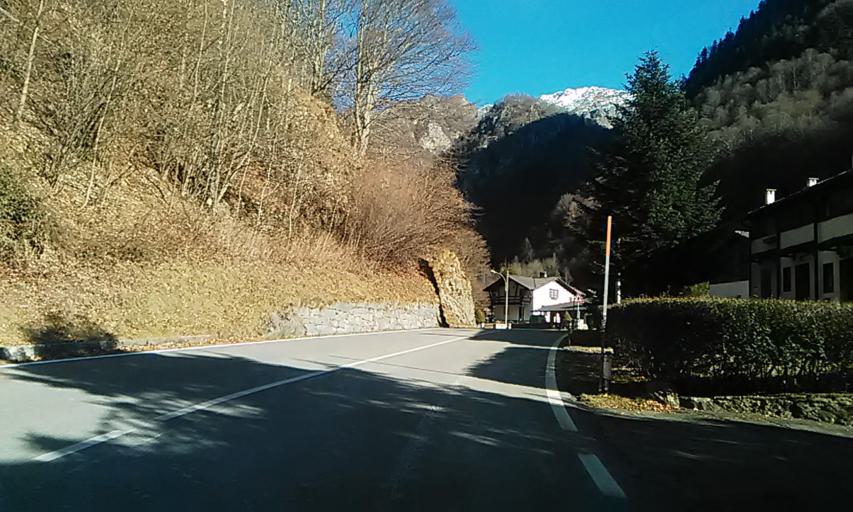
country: IT
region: Piedmont
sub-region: Provincia di Vercelli
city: Rimasco
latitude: 45.8623
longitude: 8.0644
